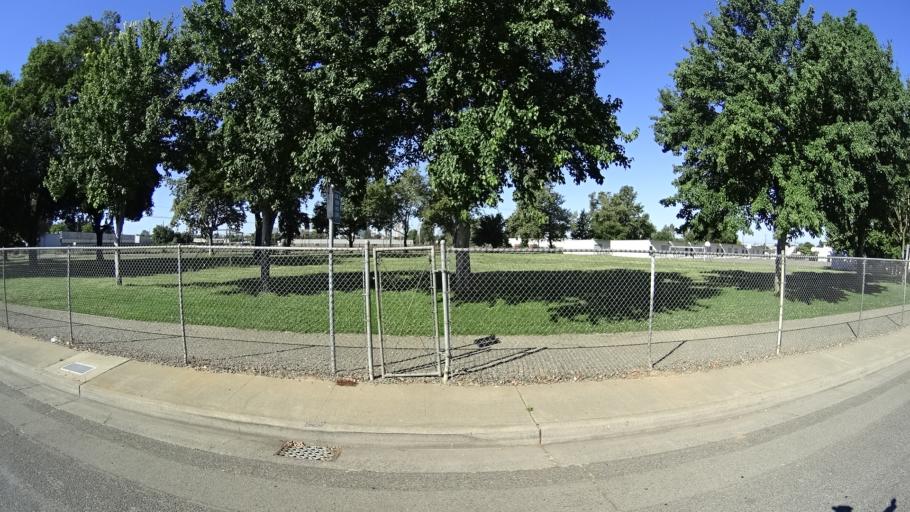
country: US
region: California
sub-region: Sacramento County
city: Sacramento
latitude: 38.5963
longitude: -121.4814
